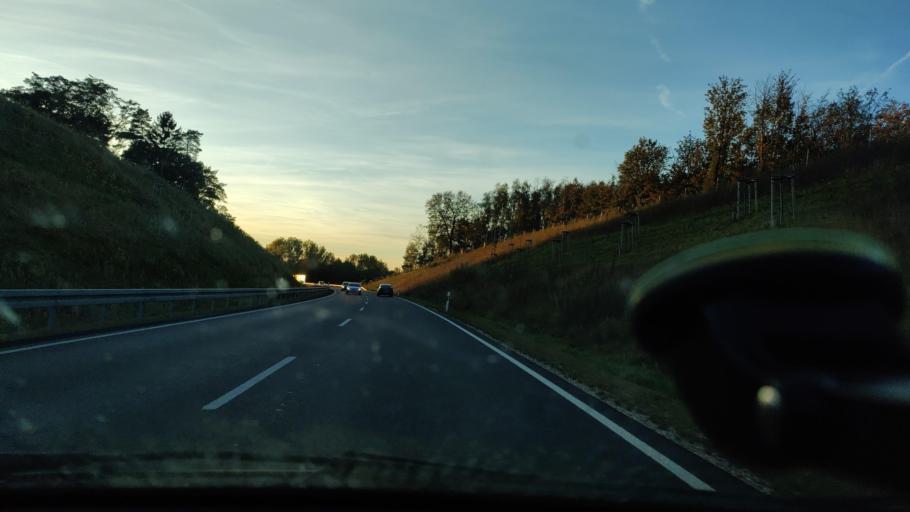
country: DE
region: North Rhine-Westphalia
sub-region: Regierungsbezirk Koln
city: Wassenberg
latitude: 51.0885
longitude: 6.1812
